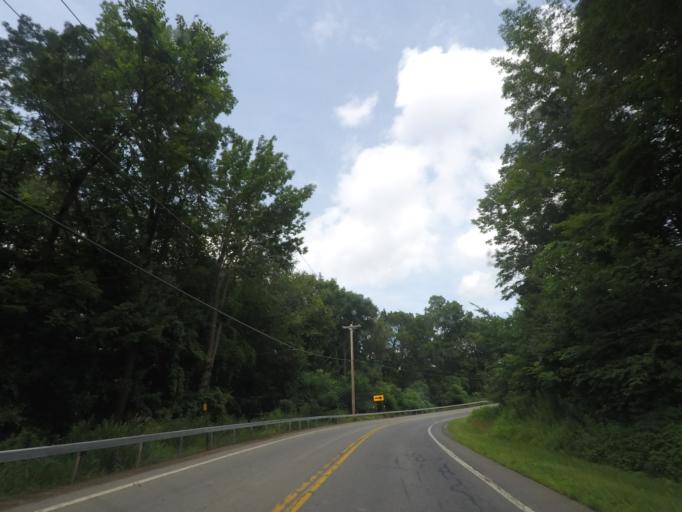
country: US
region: New York
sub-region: Saratoga County
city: Stillwater
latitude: 43.0250
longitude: -73.6854
